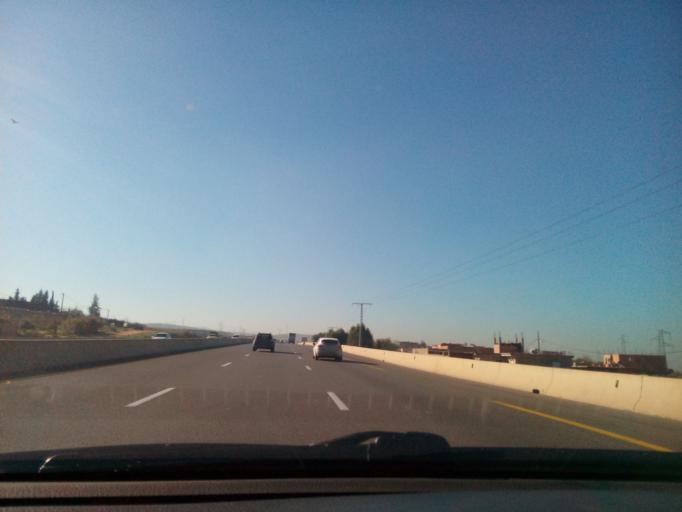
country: DZ
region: Chlef
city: Oued Sly
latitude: 36.0824
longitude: 1.1859
